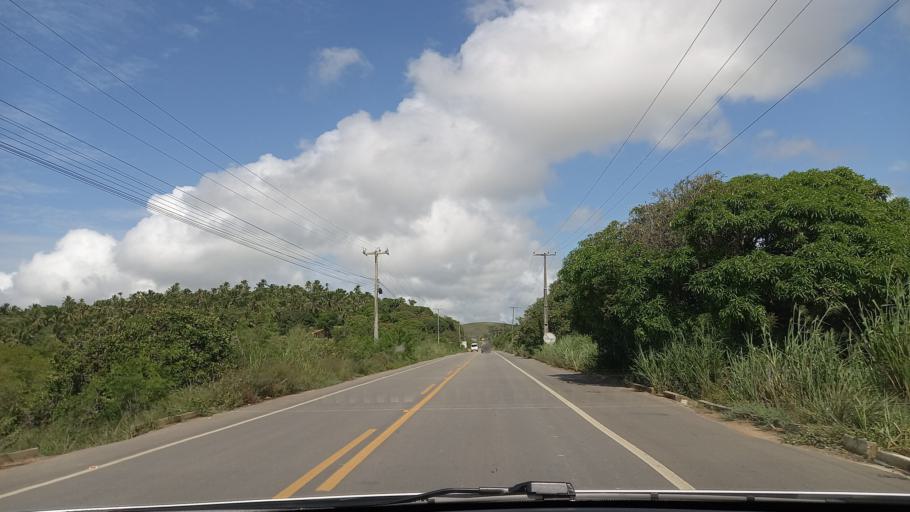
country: BR
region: Alagoas
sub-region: Maragogi
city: Maragogi
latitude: -8.9962
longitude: -35.2118
